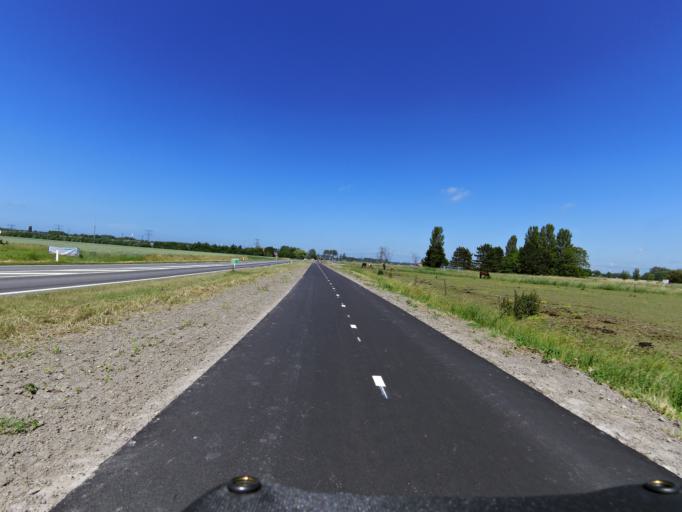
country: NL
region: South Holland
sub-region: Gemeente Brielle
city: Brielle
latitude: 51.9060
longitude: 4.1177
